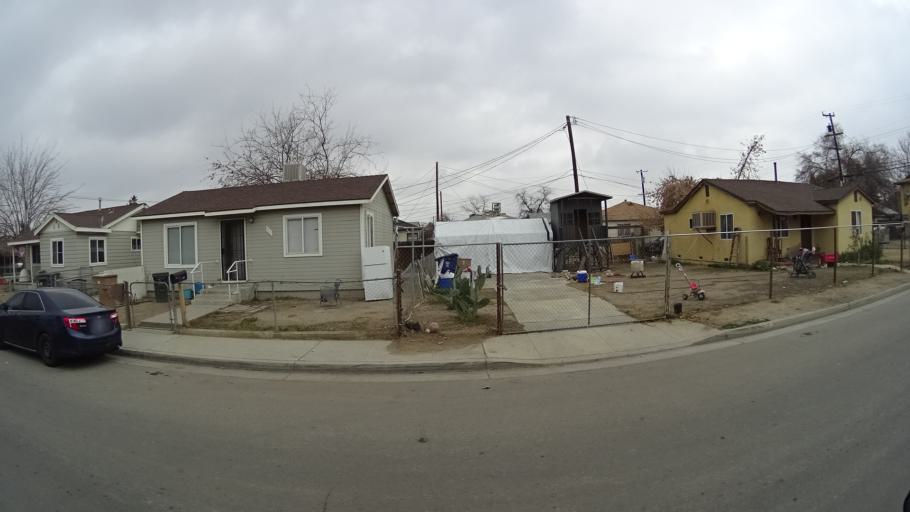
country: US
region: California
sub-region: Kern County
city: Bakersfield
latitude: 35.3881
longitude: -119.0087
